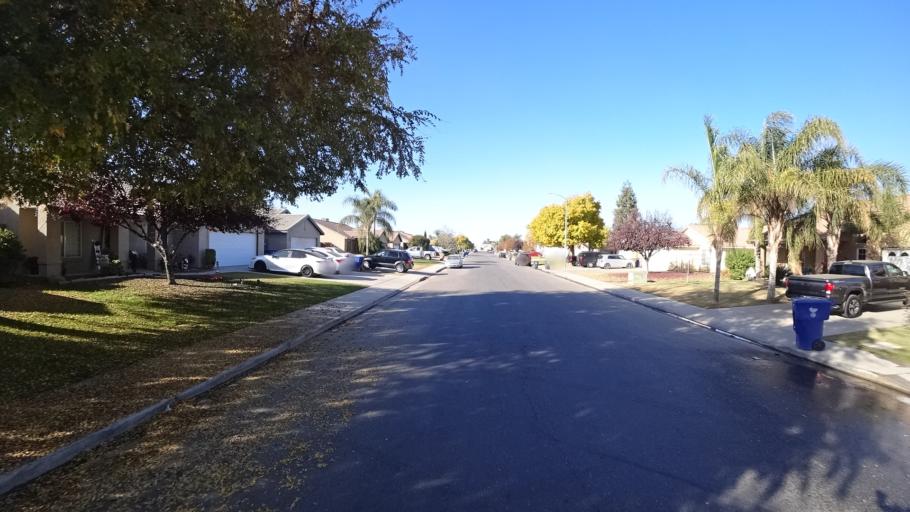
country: US
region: California
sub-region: Kern County
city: Greenfield
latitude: 35.2722
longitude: -119.0397
